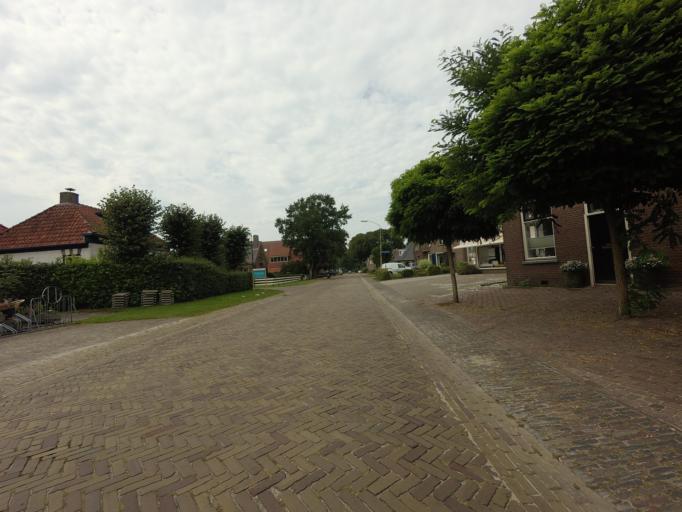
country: NL
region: Drenthe
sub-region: Gemeente Westerveld
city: Dwingeloo
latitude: 52.8318
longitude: 6.3719
